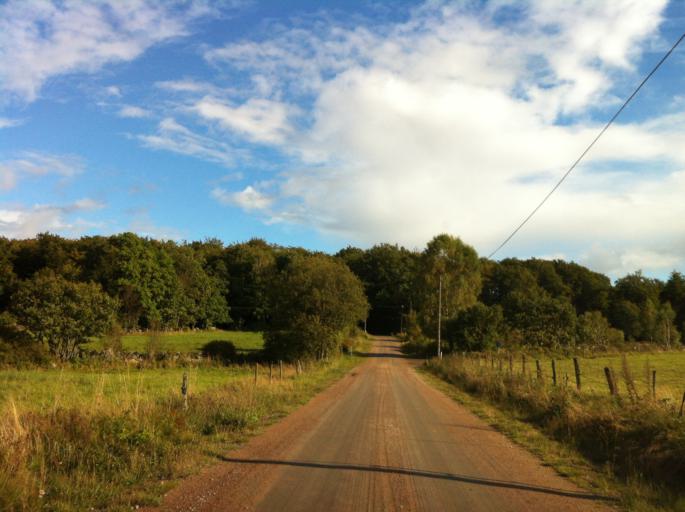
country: SE
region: Skane
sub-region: Hassleholms Kommun
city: Sosdala
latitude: 56.1334
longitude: 13.5744
